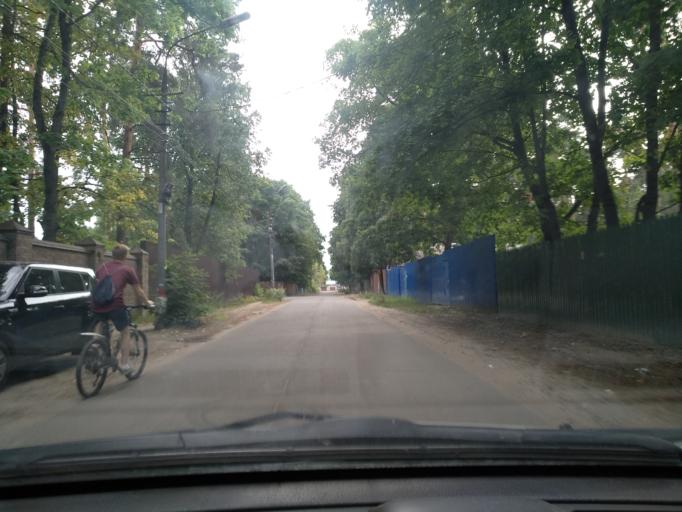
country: RU
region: Moskovskaya
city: Il'inskiy
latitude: 55.6113
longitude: 38.1021
